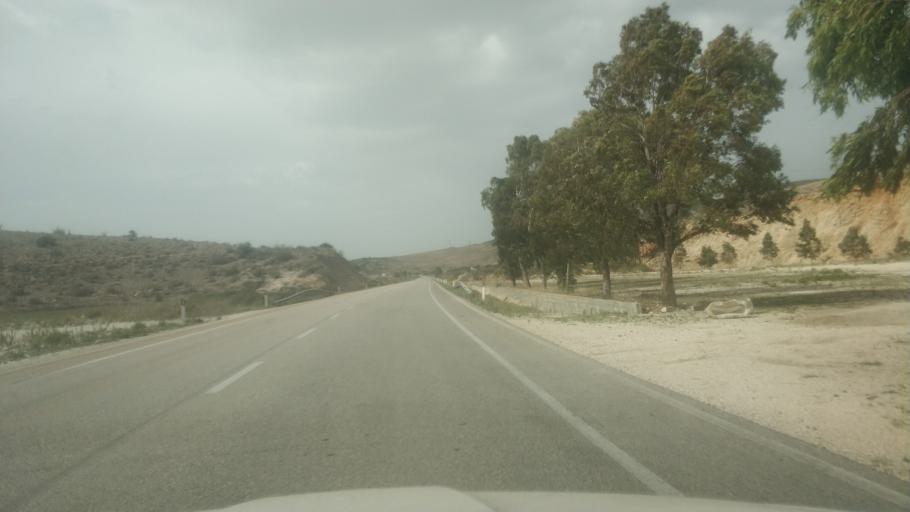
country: AL
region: Gjirokaster
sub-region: Rrethi i Tepelenes
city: Memaliaj
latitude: 40.3570
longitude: 19.9342
